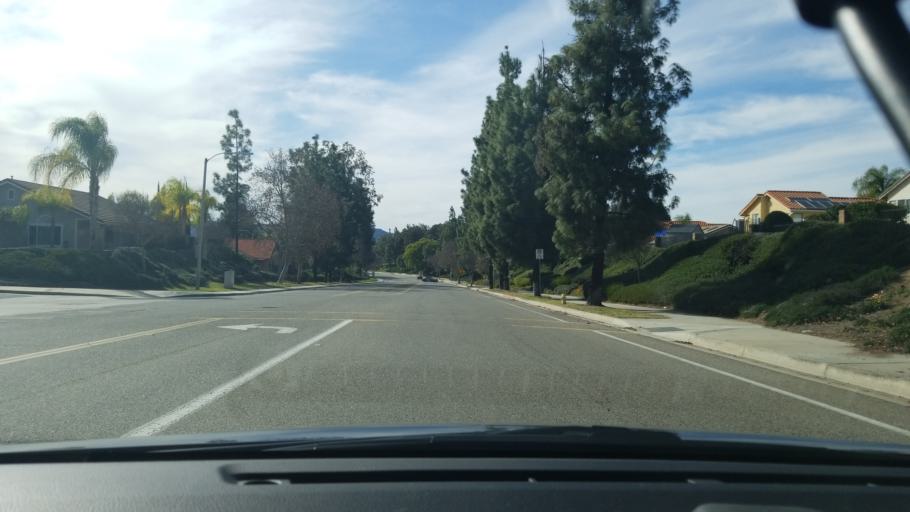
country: US
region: California
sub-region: Riverside County
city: Murrieta Hot Springs
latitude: 33.5632
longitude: -117.1732
